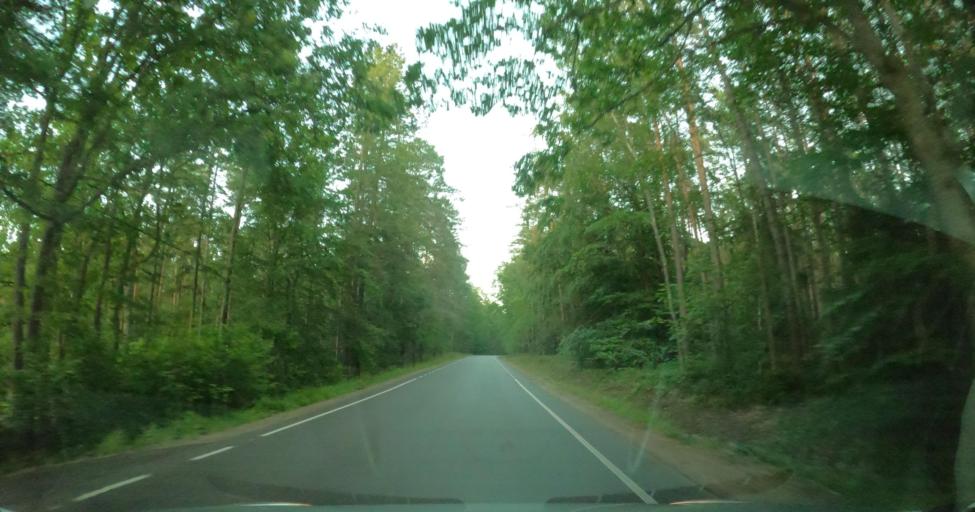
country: PL
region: Pomeranian Voivodeship
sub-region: Powiat leborski
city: Lebork
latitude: 54.5184
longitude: 17.7879
